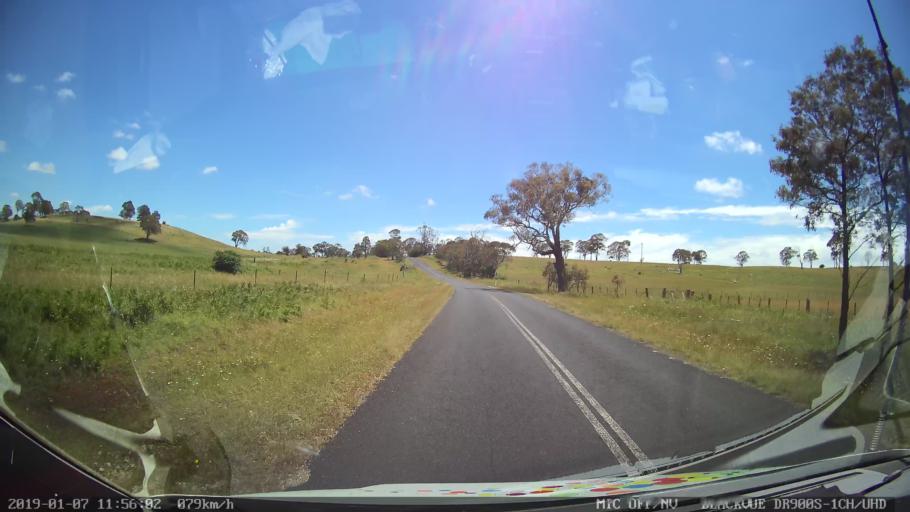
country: AU
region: New South Wales
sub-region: Guyra
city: Guyra
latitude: -30.2790
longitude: 151.6735
